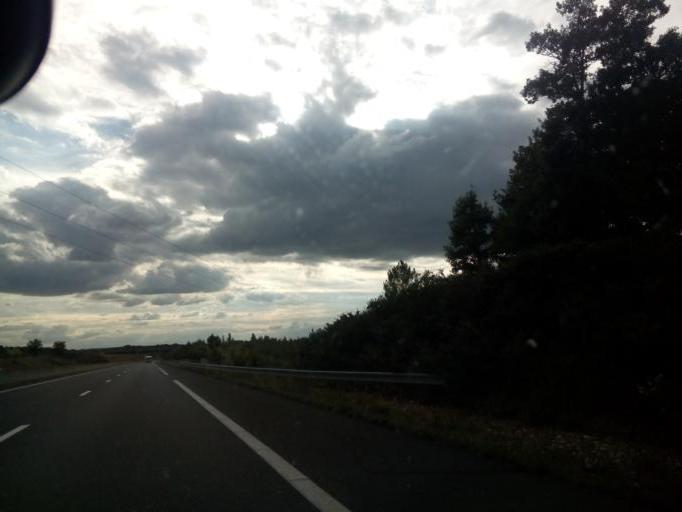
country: FR
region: Centre
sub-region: Departement d'Indre-et-Loire
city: Civray-de-Touraine
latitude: 47.2875
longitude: 1.0798
